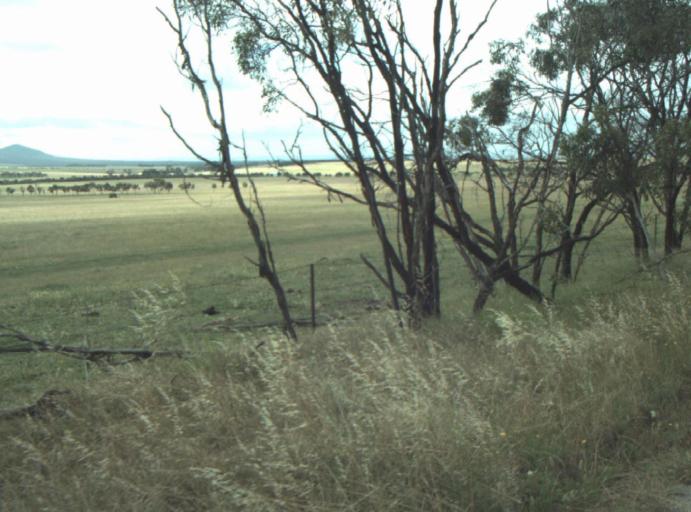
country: AU
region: Victoria
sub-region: Greater Geelong
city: Lara
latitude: -37.8739
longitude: 144.3227
